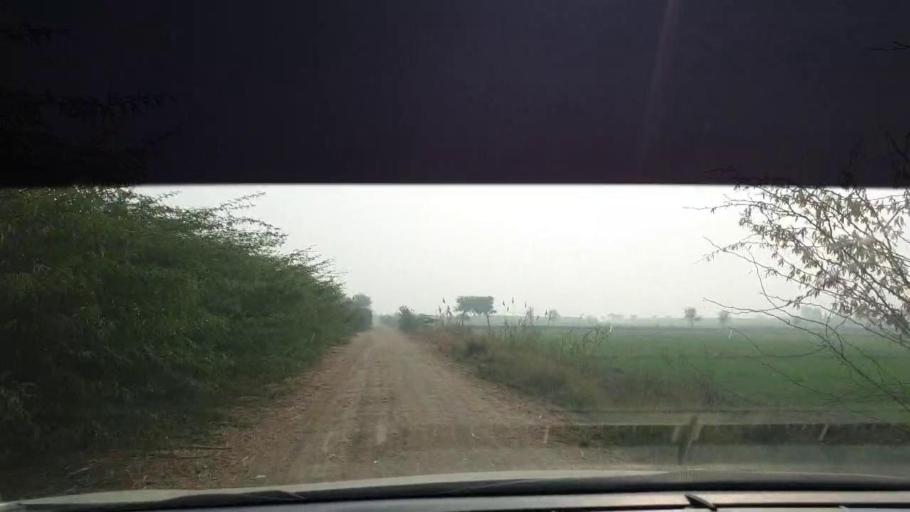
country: PK
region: Sindh
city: Berani
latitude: 25.8295
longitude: 68.8352
